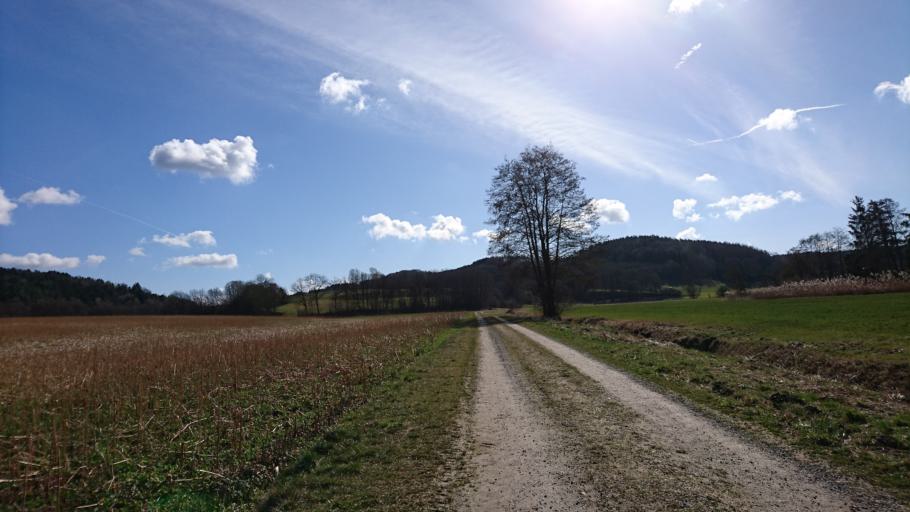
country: DE
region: Bavaria
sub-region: Swabia
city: Altenmunster
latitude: 48.4472
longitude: 10.5974
